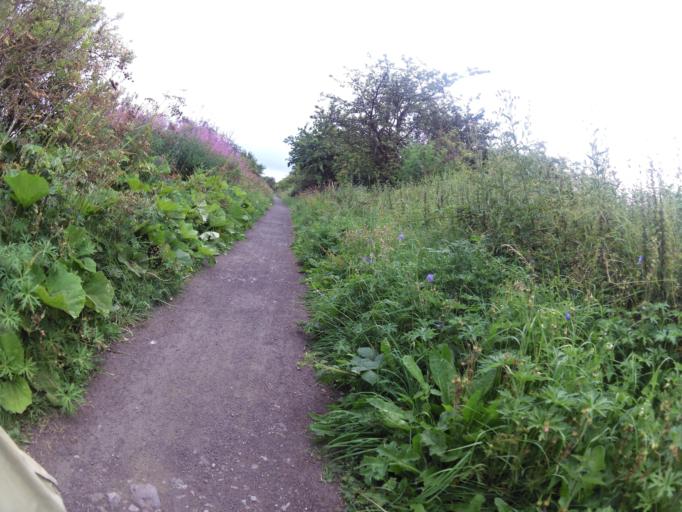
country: GB
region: Scotland
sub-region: Edinburgh
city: Kirkliston
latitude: 55.9523
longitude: -3.4007
